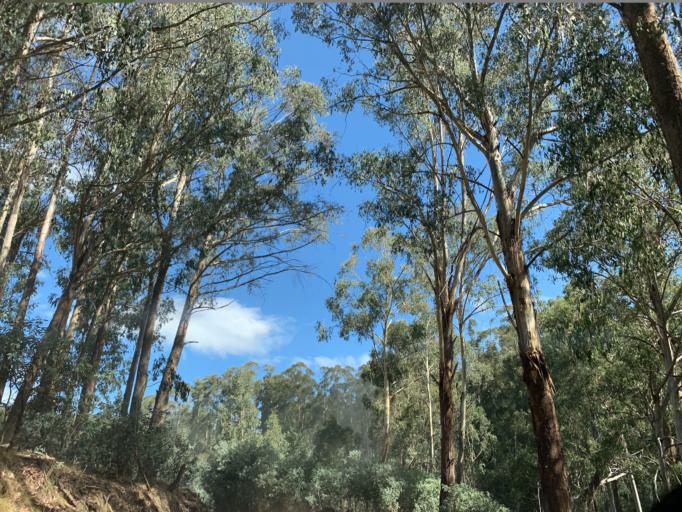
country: AU
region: Victoria
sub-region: Mansfield
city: Mansfield
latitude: -37.0976
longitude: 146.4638
